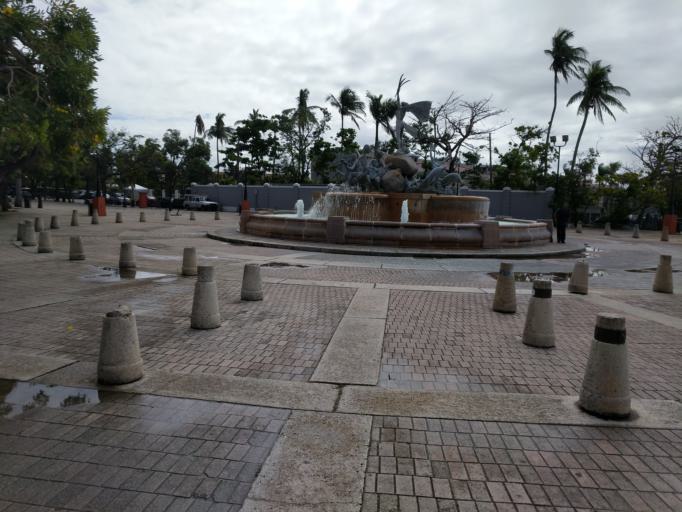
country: PR
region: San Juan
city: San Juan
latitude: 18.4635
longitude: -66.1187
